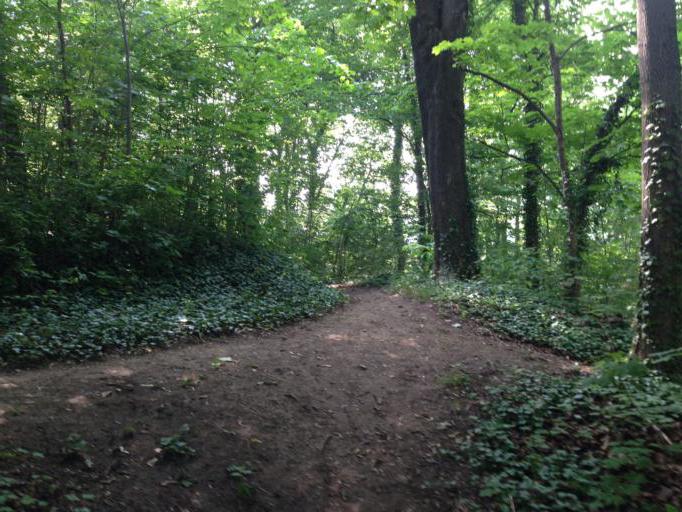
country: DE
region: Thuringia
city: Ranis
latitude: 50.6637
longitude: 11.5665
